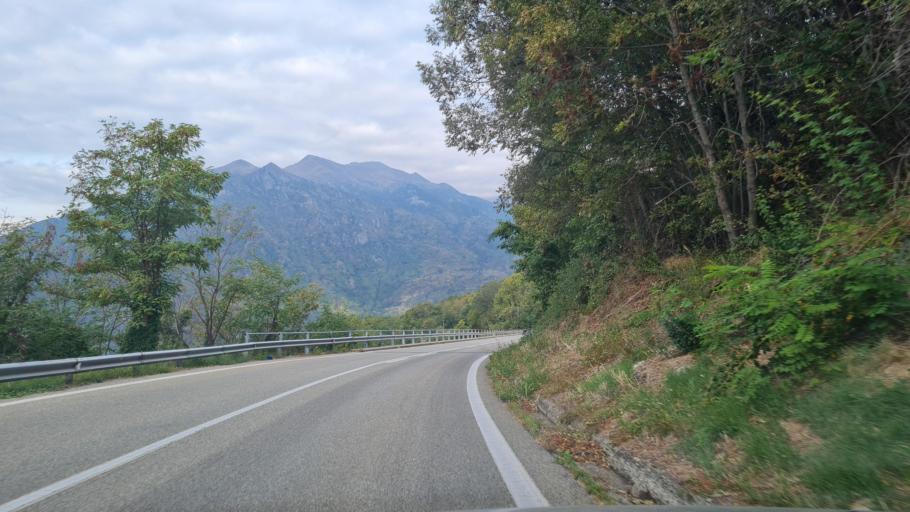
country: IT
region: Piedmont
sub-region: Provincia di Torino
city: Andrate
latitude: 45.5204
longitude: 7.8745
